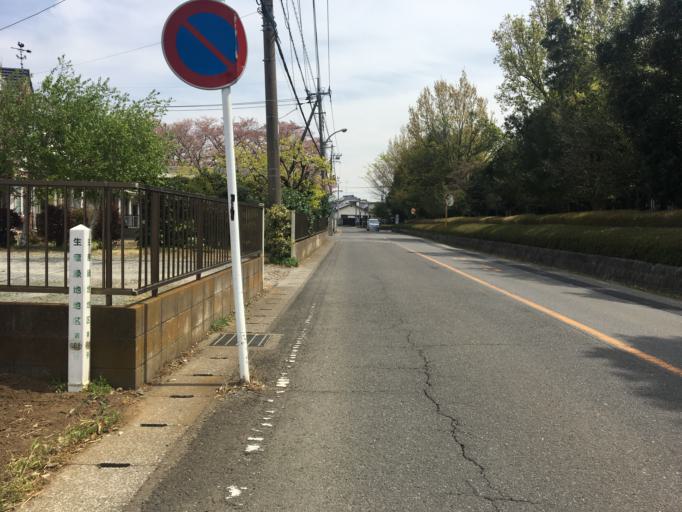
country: JP
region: Saitama
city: Shiki
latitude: 35.8466
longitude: 139.5613
